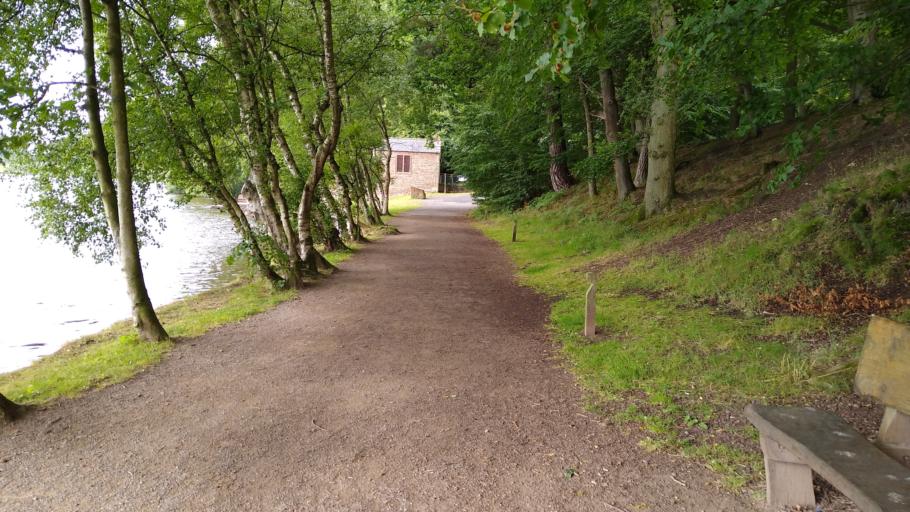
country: GB
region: England
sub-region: Cumbria
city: Brampton
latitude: 54.9242
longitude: -2.7122
